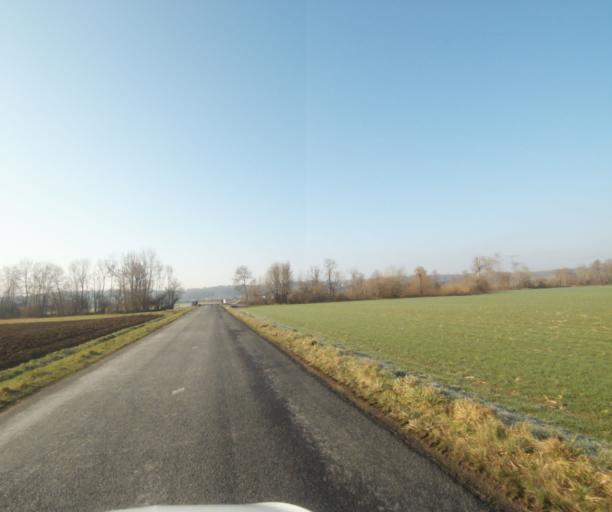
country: FR
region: Champagne-Ardenne
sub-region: Departement de la Haute-Marne
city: Wassy
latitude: 48.5162
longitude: 4.9321
